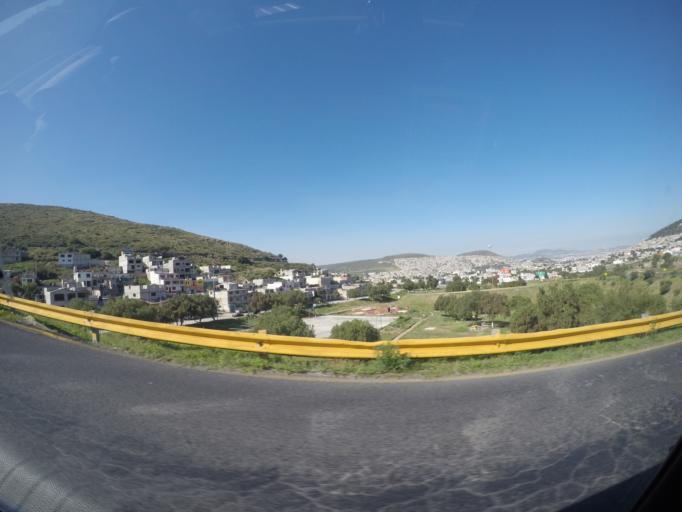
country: MX
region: Hidalgo
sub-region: Mineral de la Reforma
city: Rio de la Soledad
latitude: 20.1195
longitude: -98.7087
